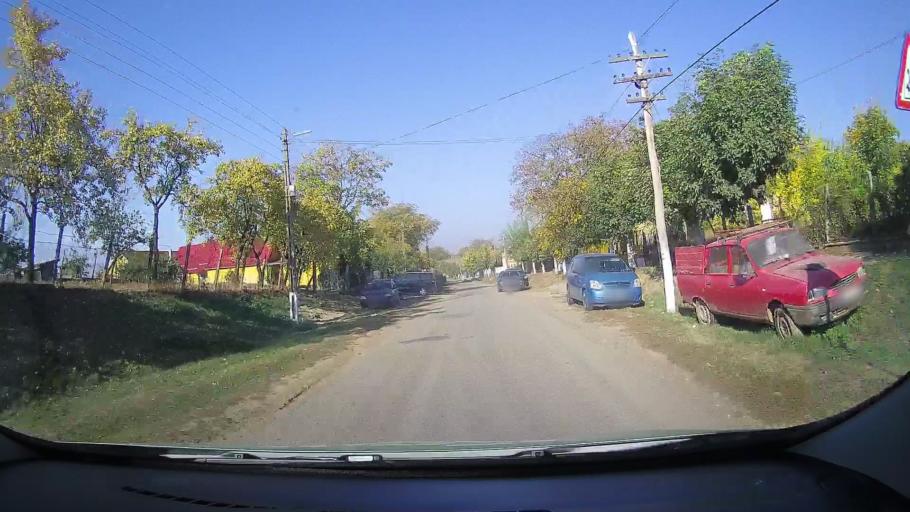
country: RO
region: Satu Mare
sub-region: Comuna Sauca
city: Sauca
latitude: 47.4705
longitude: 22.4919
